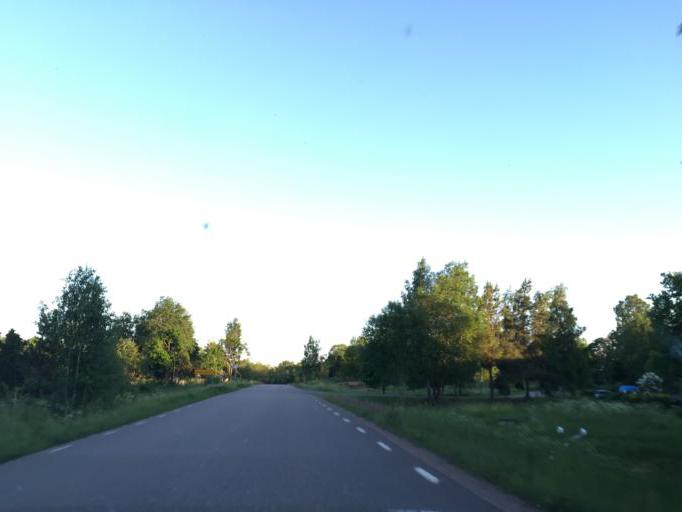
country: SE
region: Soedermanland
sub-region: Eskilstuna Kommun
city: Torshalla
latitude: 59.5279
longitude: 16.4416
